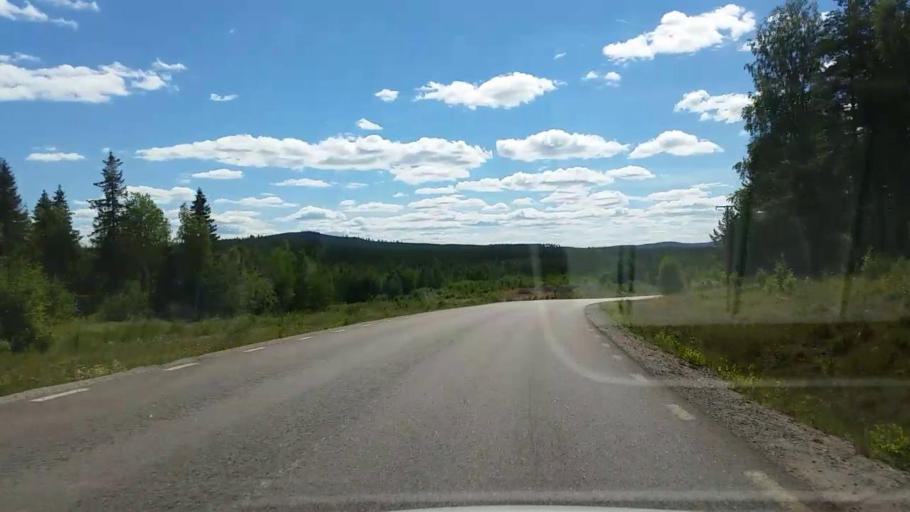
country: SE
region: Dalarna
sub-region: Faluns Kommun
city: Svardsjo
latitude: 61.0155
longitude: 15.7549
